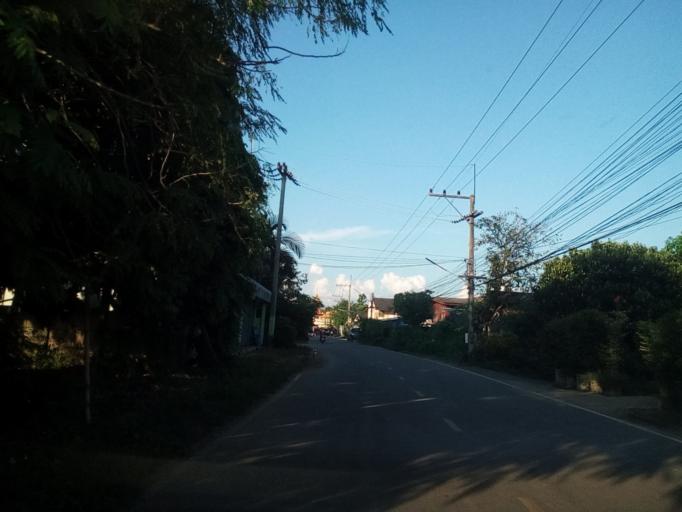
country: TH
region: Lamphun
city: Ban Thi
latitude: 18.6313
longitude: 99.0523
